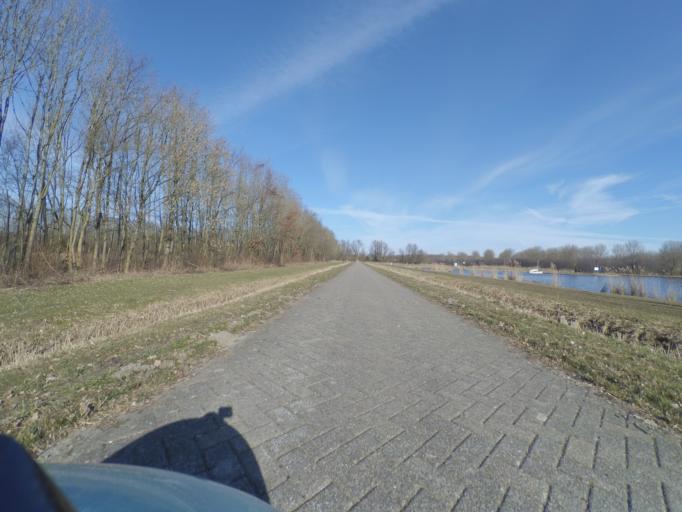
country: NL
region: Flevoland
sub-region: Gemeente Almere
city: Almere Stad
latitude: 52.4022
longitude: 5.2254
